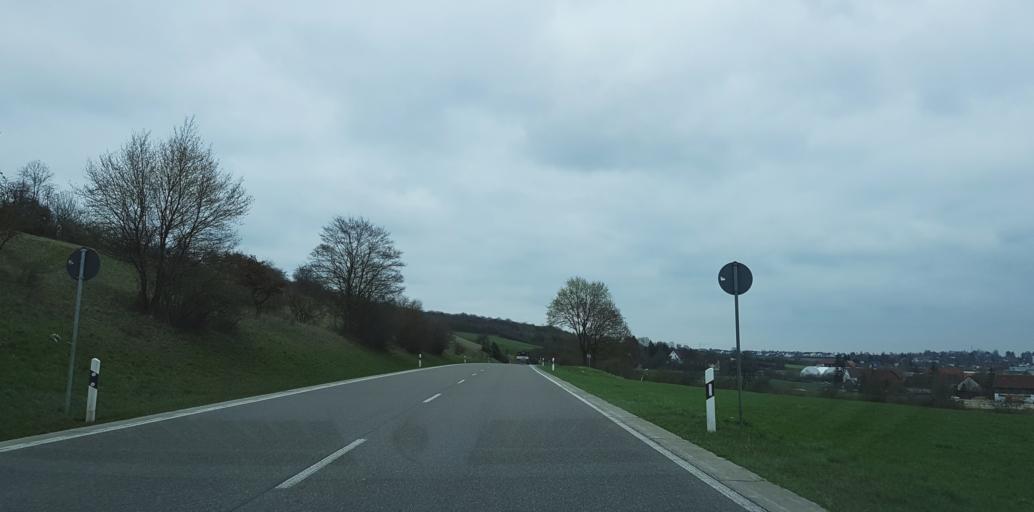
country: DE
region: Baden-Wuerttemberg
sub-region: Tuebingen Region
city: Ehingen
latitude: 48.3025
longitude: 9.7270
